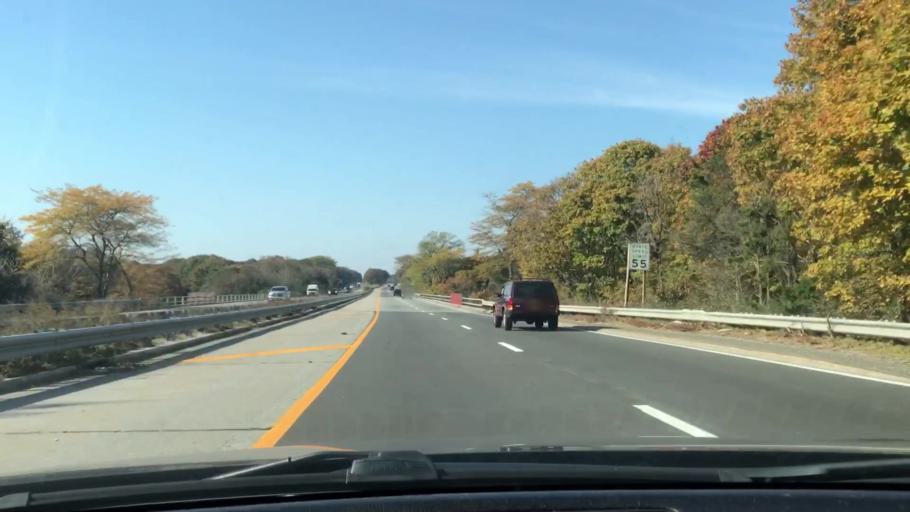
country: US
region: New York
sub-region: Suffolk County
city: Hampton Bays
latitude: 40.8896
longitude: -72.5007
